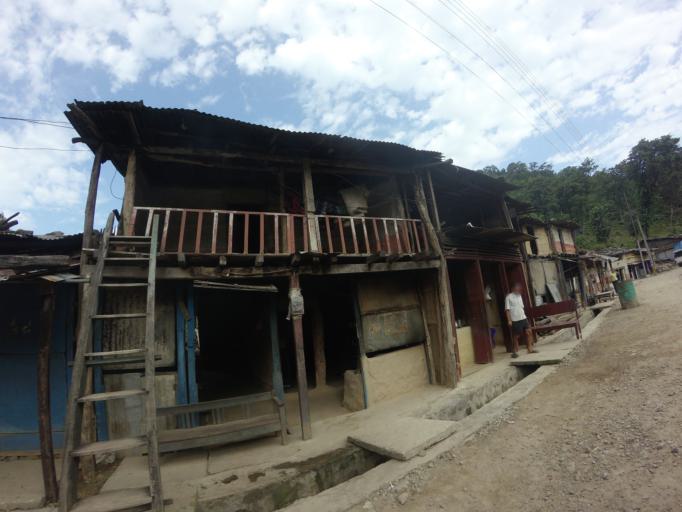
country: NP
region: Far Western
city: Tikapur
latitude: 28.6469
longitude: 81.2845
